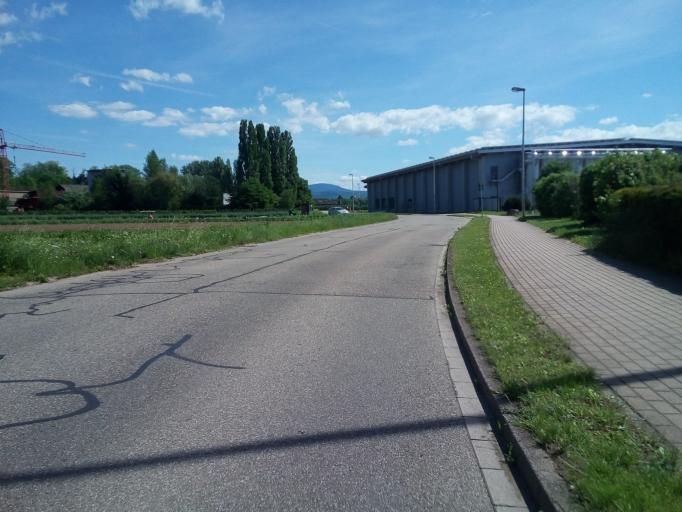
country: DE
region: Baden-Wuerttemberg
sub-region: Freiburg Region
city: Renchen
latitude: 48.5795
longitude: 8.0124
